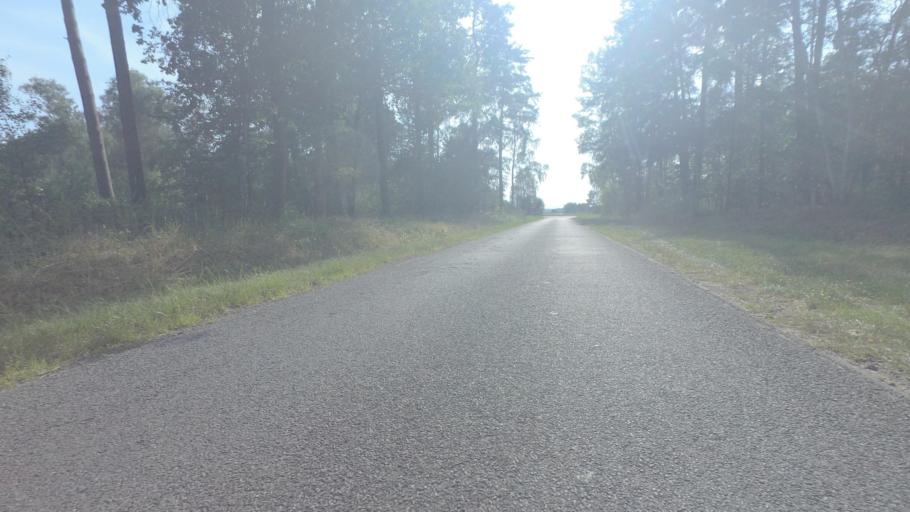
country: DE
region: Brandenburg
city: Wittstock
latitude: 53.2693
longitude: 12.4577
